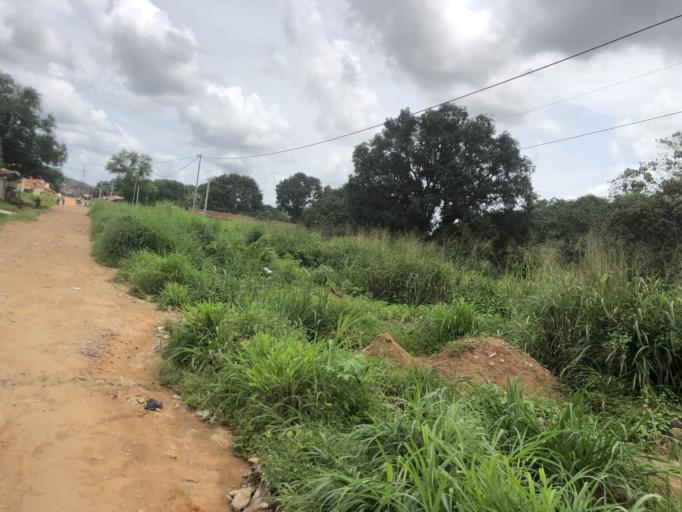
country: SL
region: Northern Province
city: Makeni
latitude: 8.8784
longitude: -12.0541
